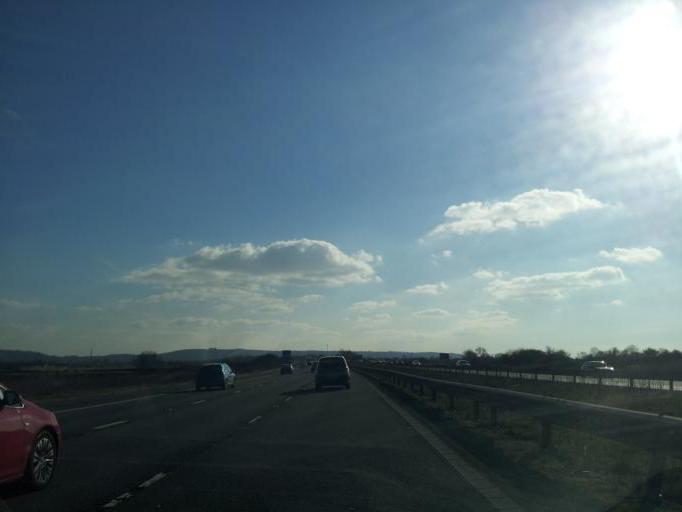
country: GB
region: England
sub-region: North Somerset
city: St. Georges
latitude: 51.3732
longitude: -2.8863
